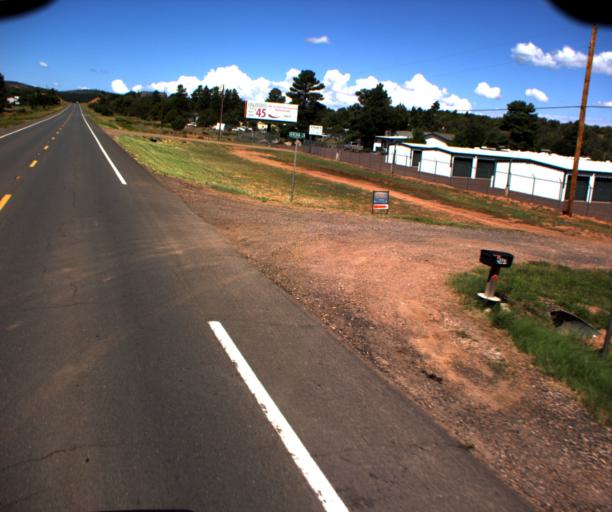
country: US
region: Arizona
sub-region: Navajo County
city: Linden
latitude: 34.2854
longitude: -110.1426
